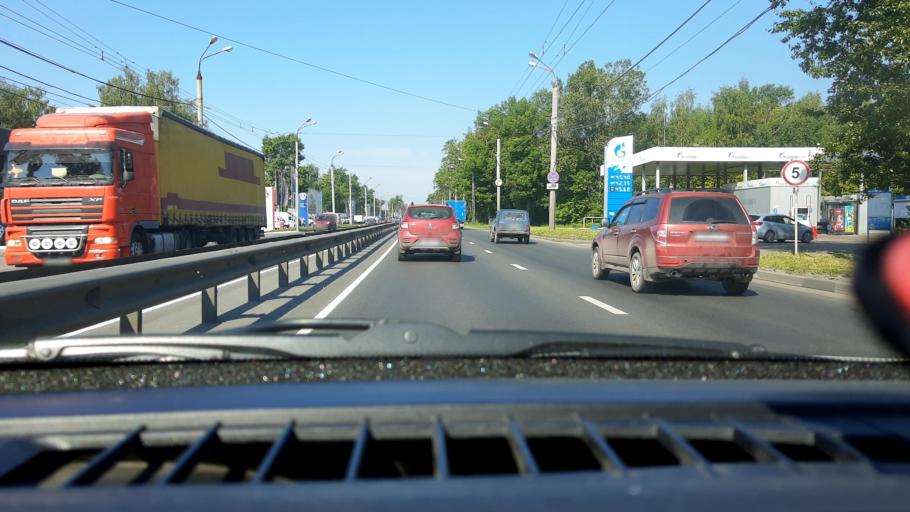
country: RU
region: Nizjnij Novgorod
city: Gorbatovka
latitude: 56.3120
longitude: 43.8475
